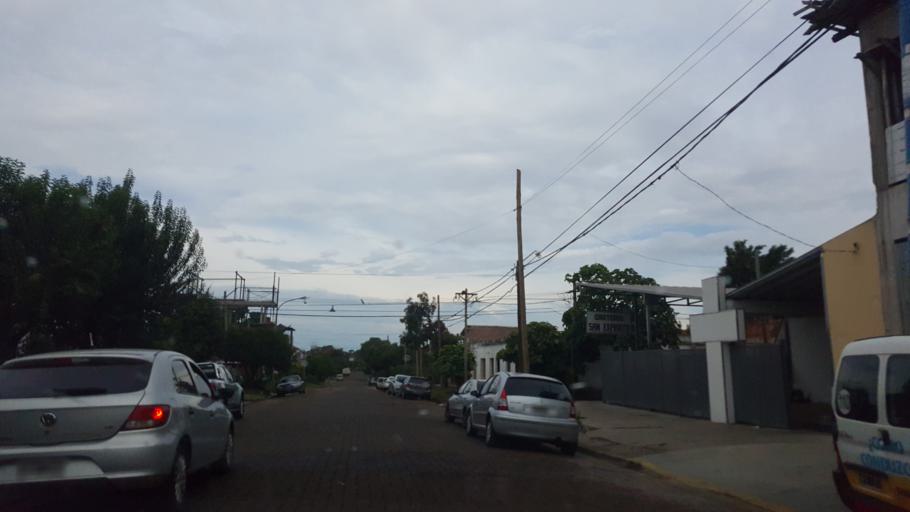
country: AR
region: Misiones
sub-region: Departamento de Capital
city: Posadas
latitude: -27.3895
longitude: -55.9004
